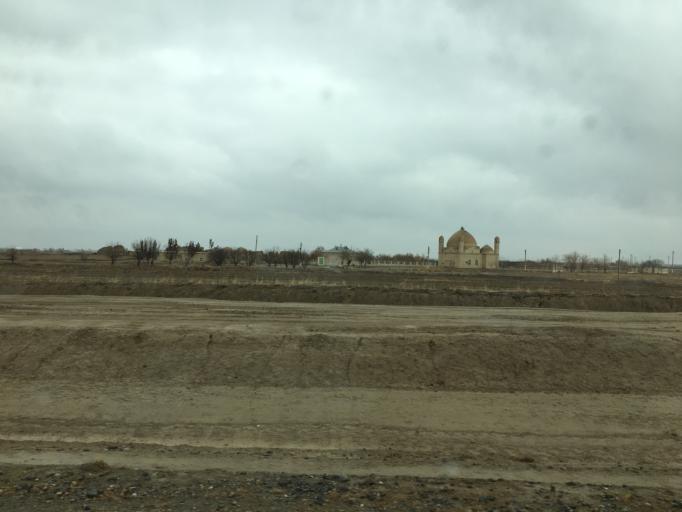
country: TM
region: Mary
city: Bayramaly
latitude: 37.4099
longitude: 62.1682
